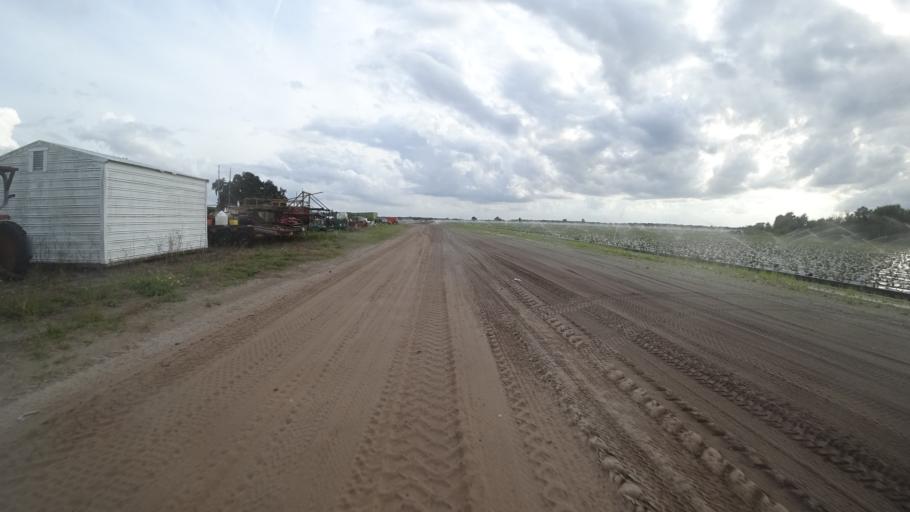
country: US
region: Florida
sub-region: Hillsborough County
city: Wimauma
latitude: 27.5777
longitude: -82.1574
